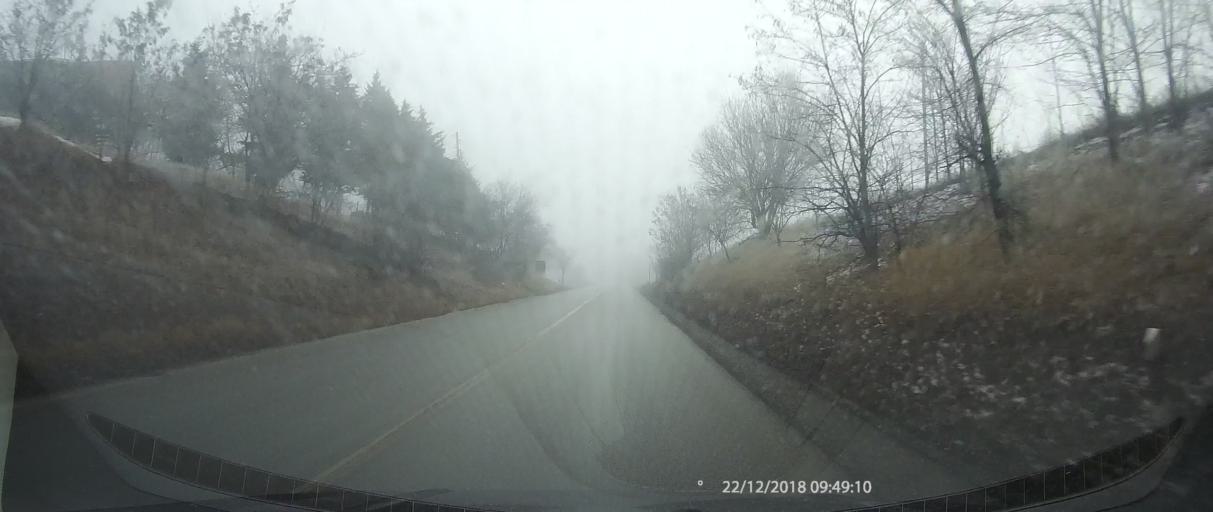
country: MK
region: Kumanovo
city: Kumanovo
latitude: 42.1689
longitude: 21.7651
